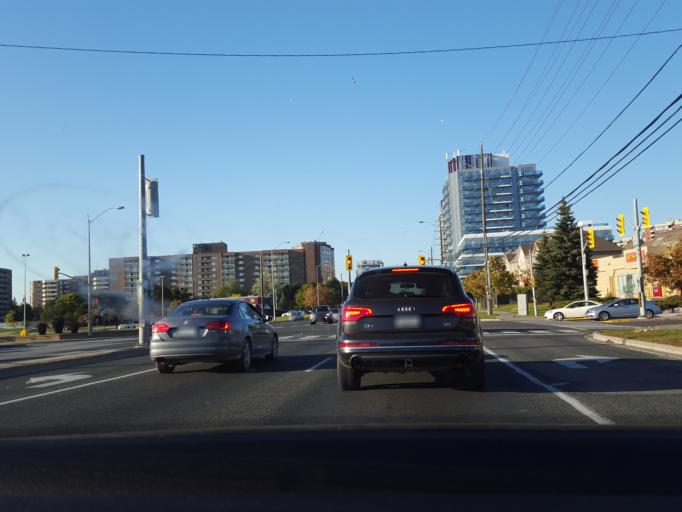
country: CA
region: Ontario
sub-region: York
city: Richmond Hill
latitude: 43.8551
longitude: -79.4334
